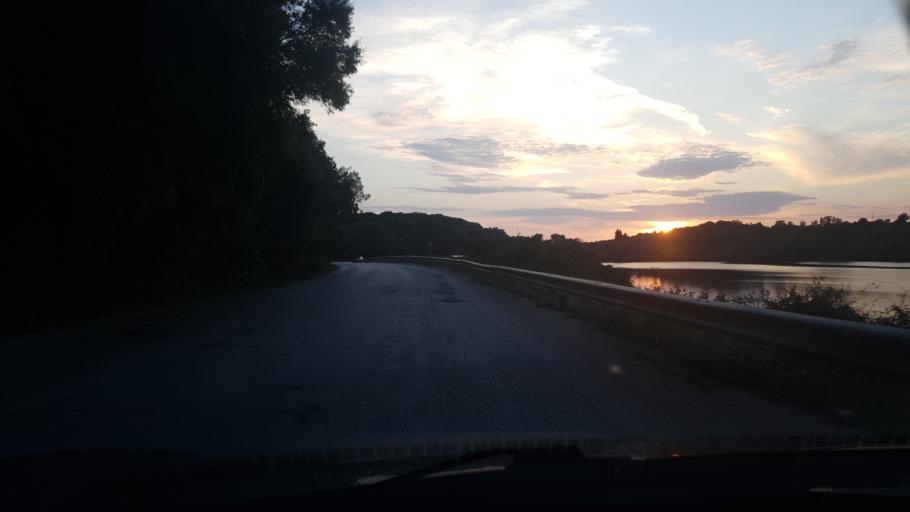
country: GR
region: West Greece
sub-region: Nomos Aitolias kai Akarnanias
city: Vonitsa
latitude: 38.9180
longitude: 20.8648
